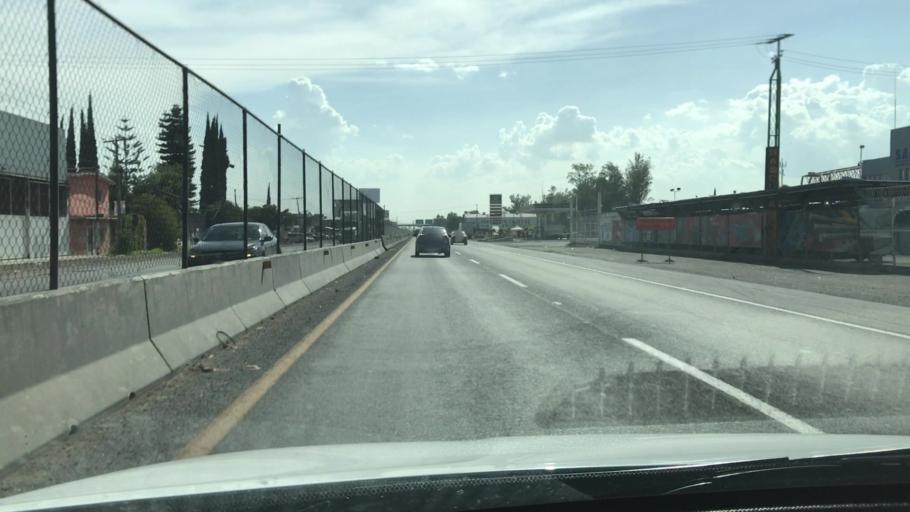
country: MX
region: Guanajuato
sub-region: Celaya
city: Colonia Pedro Maria Anaya
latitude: 20.5164
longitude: -100.8809
